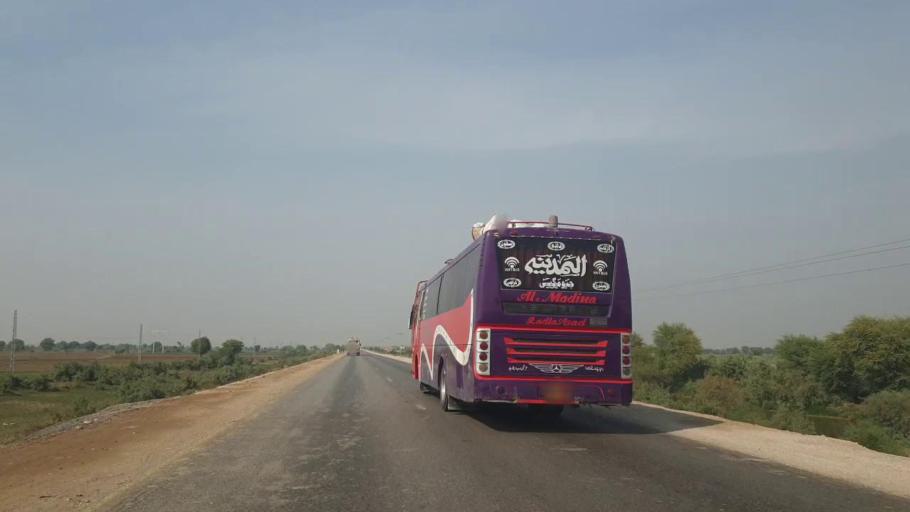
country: PK
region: Sindh
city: Sann
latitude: 26.0777
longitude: 68.0959
